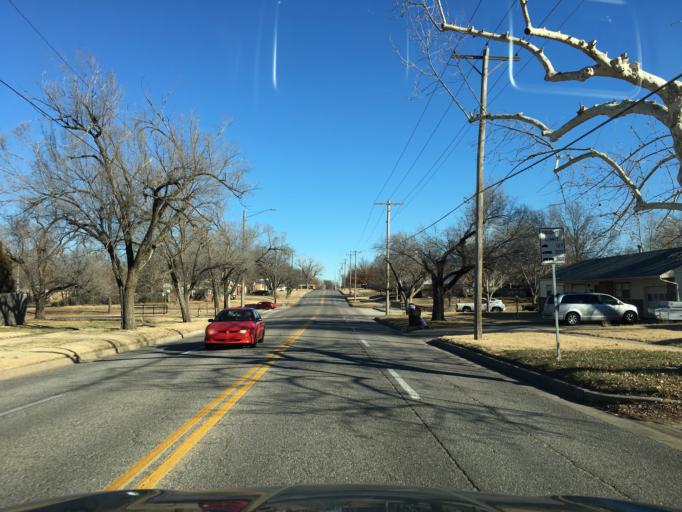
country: US
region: Kansas
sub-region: Sedgwick County
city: Wichita
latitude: 37.6719
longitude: -97.2511
